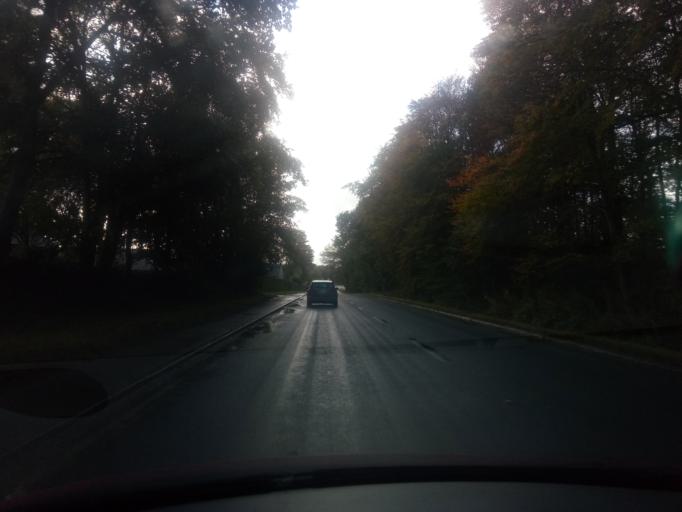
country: GB
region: England
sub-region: Cumbria
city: Carlisle
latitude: 54.9358
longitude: -2.9451
